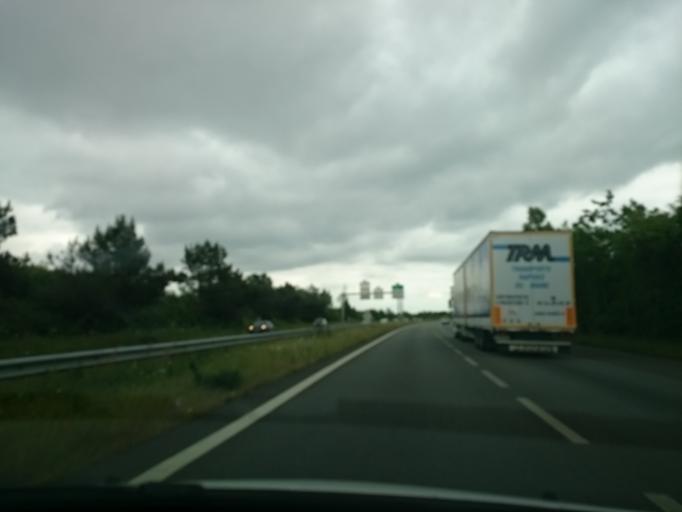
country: FR
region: Pays de la Loire
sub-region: Departement de la Loire-Atlantique
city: La Montagne
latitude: 47.1719
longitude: -1.6624
